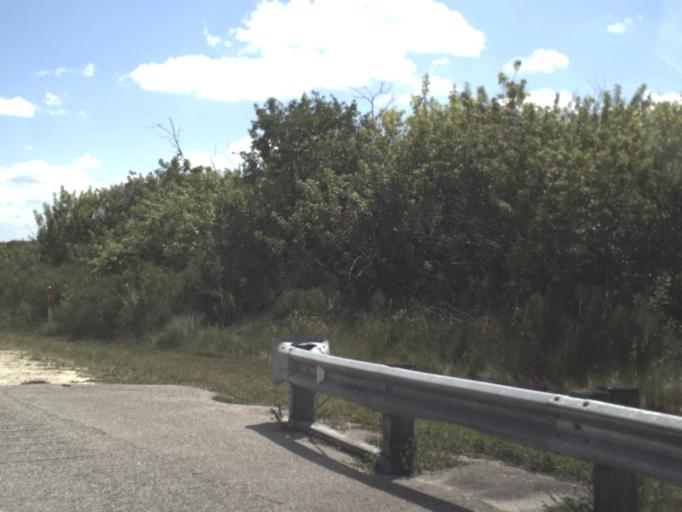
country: US
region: Florida
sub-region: Collier County
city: Marco
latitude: 25.9559
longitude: -81.4886
